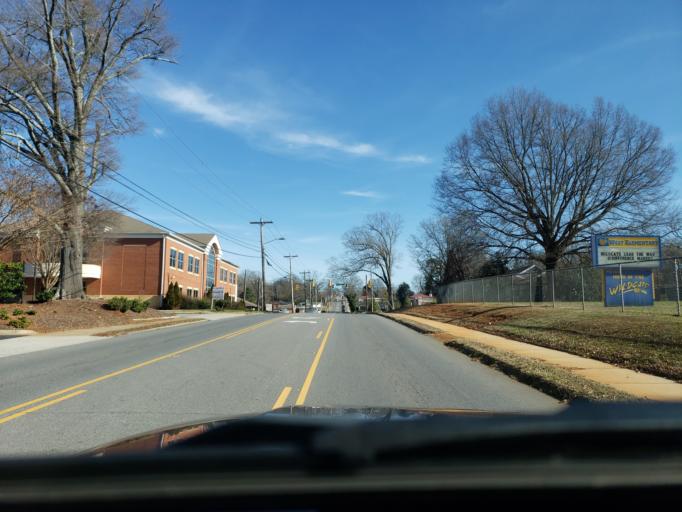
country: US
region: North Carolina
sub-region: Cleveland County
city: Kings Mountain
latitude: 35.2409
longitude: -81.3521
